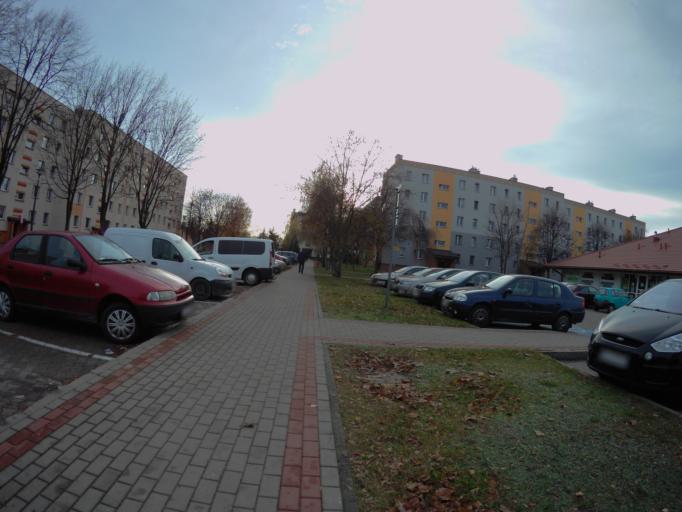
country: PL
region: Subcarpathian Voivodeship
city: Nowa Sarzyna
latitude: 50.3176
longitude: 22.3407
